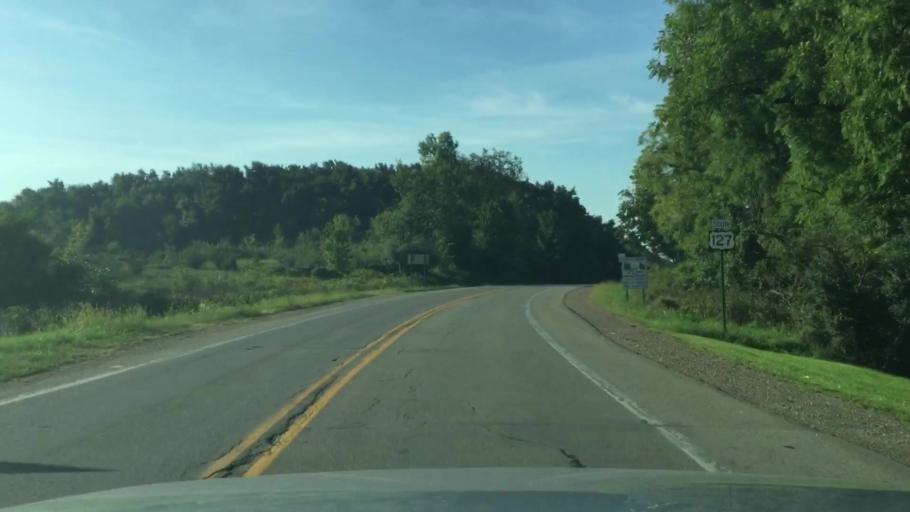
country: US
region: Michigan
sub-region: Lenawee County
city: Manitou Beach-Devils Lake
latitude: 42.0386
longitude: -84.3506
